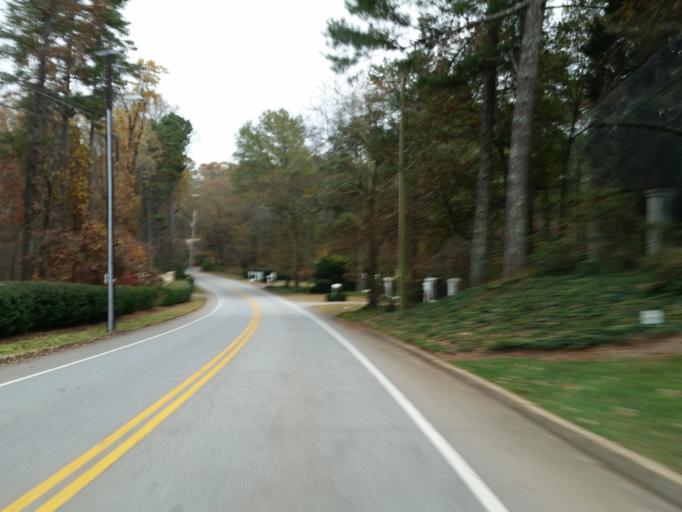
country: US
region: Georgia
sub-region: Cobb County
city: Vinings
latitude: 33.8935
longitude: -84.4302
